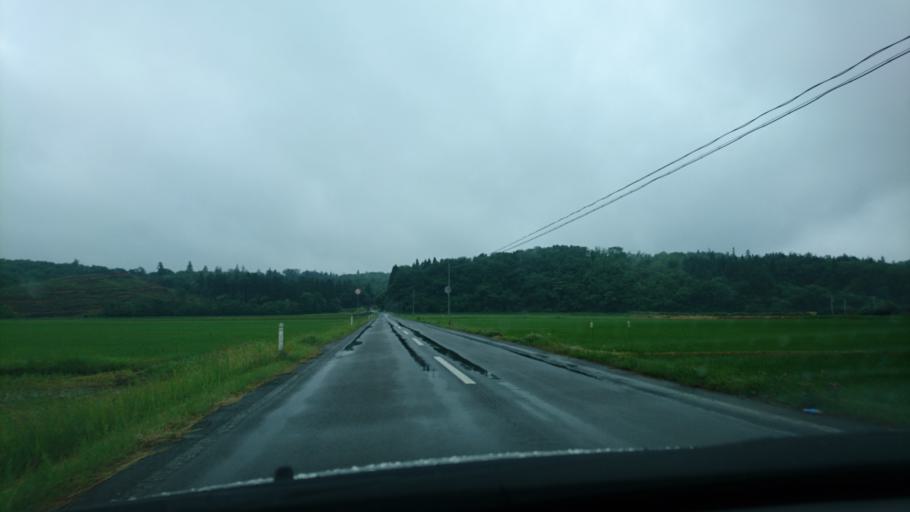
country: JP
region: Iwate
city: Ichinoseki
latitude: 38.9243
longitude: 141.0242
